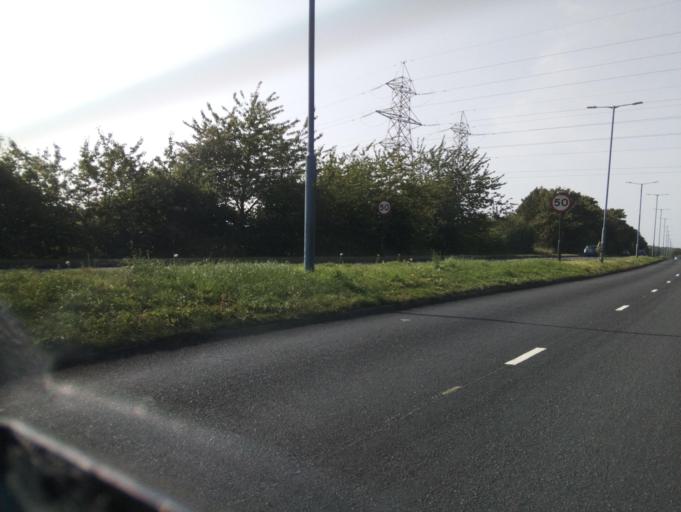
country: GB
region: England
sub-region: Sandwell
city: West Bromwich
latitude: 52.5412
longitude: -1.9619
